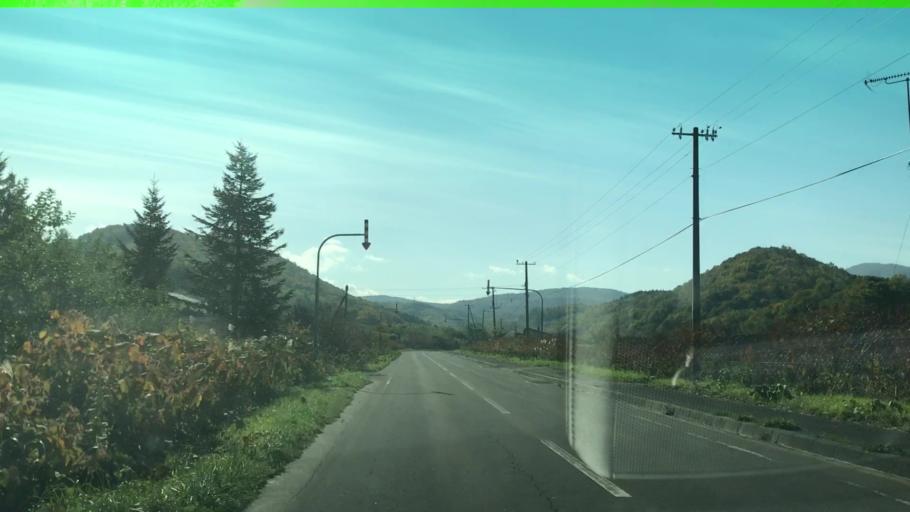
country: JP
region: Hokkaido
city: Yoichi
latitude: 43.1586
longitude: 140.8220
